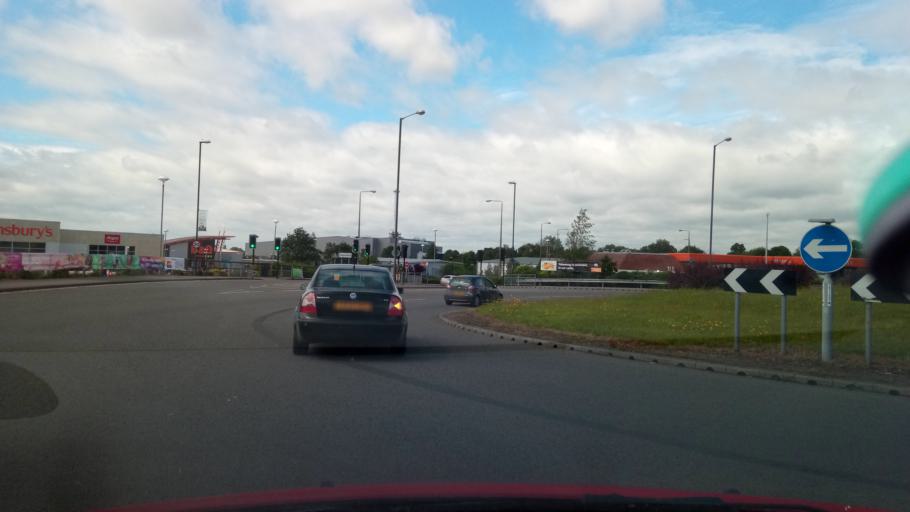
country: GB
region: England
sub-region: Derby
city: Derby
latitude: 52.8963
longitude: -1.4713
